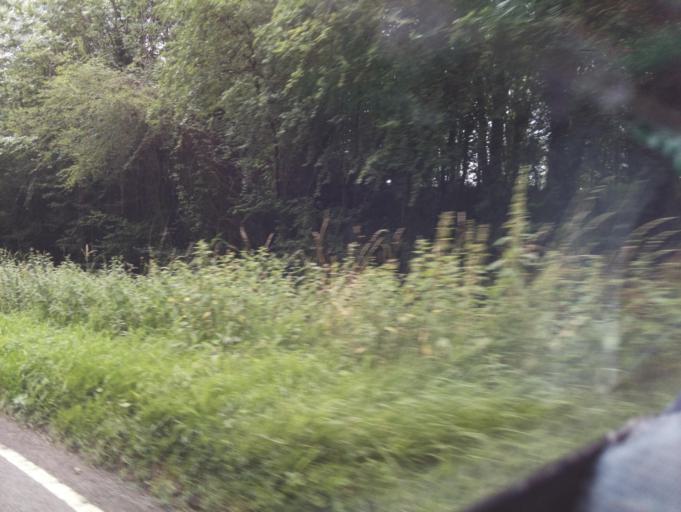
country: GB
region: England
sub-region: Northamptonshire
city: Corby
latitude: 52.5157
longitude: -0.6683
